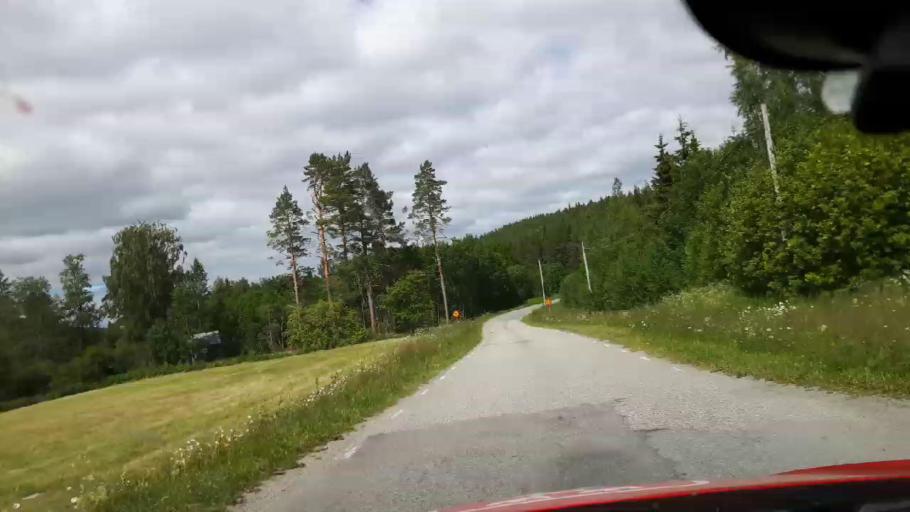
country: SE
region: Jaemtland
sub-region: Braecke Kommun
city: Braecke
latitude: 62.8540
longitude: 15.2898
